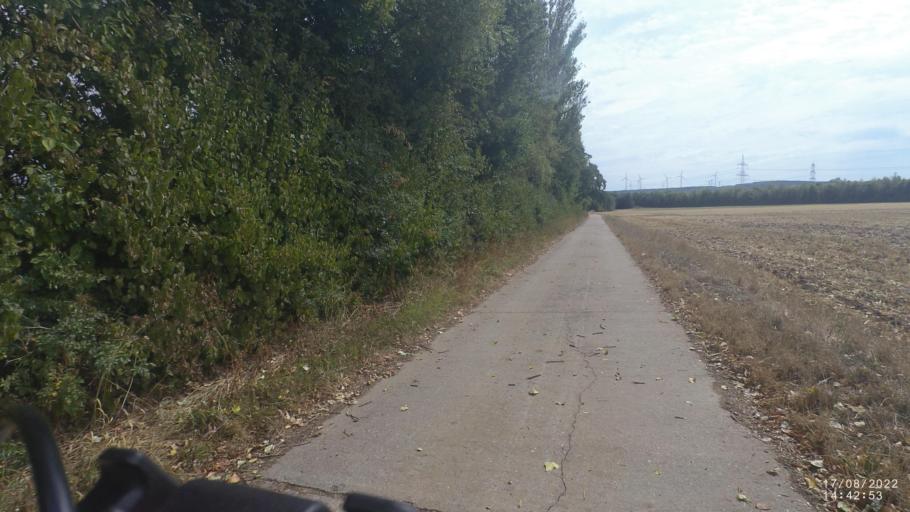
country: DE
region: Rheinland-Pfalz
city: Armsheim
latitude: 49.8028
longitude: 8.0616
